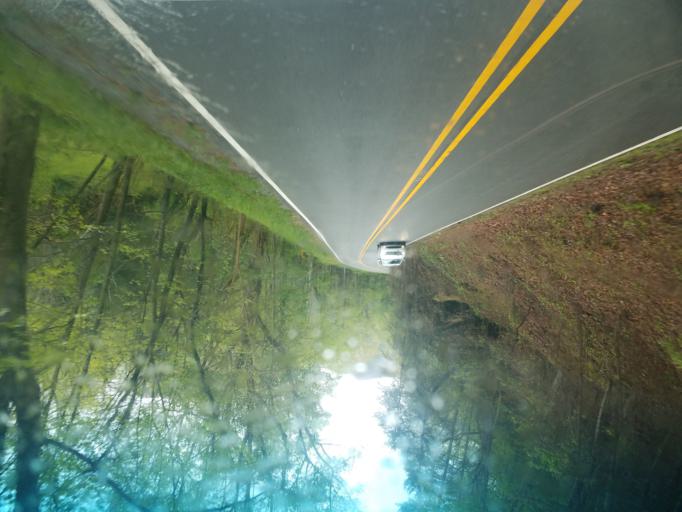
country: US
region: Tennessee
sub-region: Johnson County
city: Mountain City
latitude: 36.6250
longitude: -81.7628
